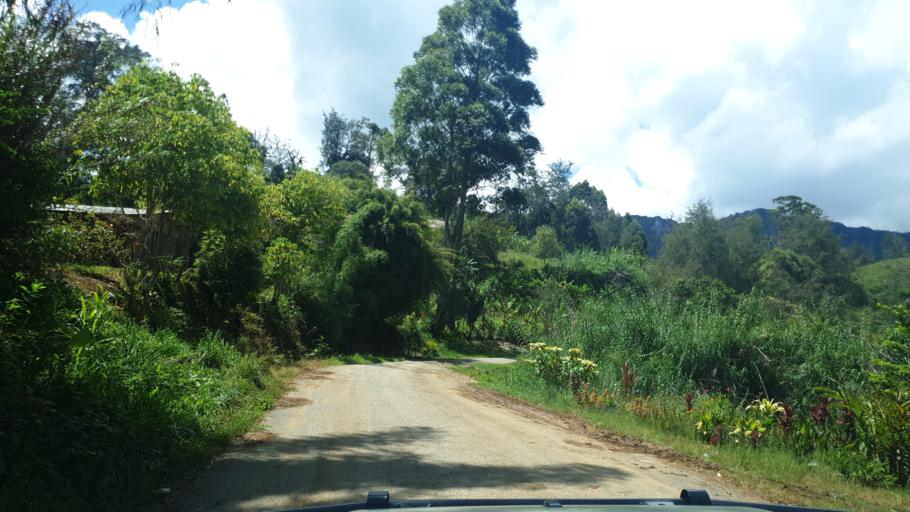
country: PG
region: Chimbu
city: Kundiawa
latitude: -6.1450
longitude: 145.1327
